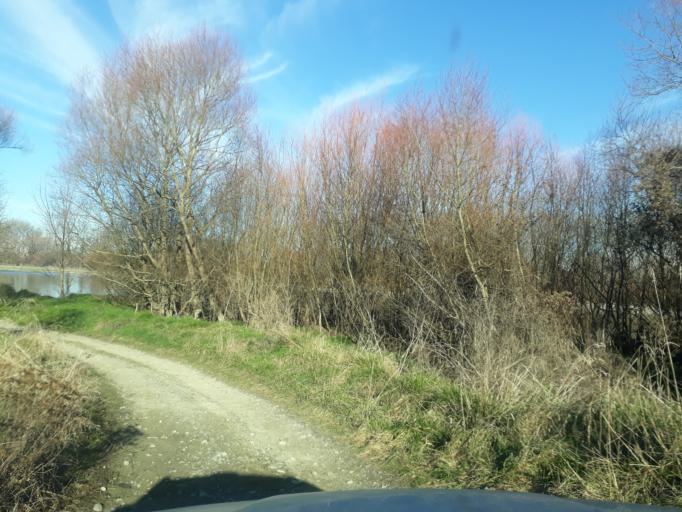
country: NZ
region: Canterbury
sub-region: Timaru District
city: Timaru
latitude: -44.2699
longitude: 171.3324
